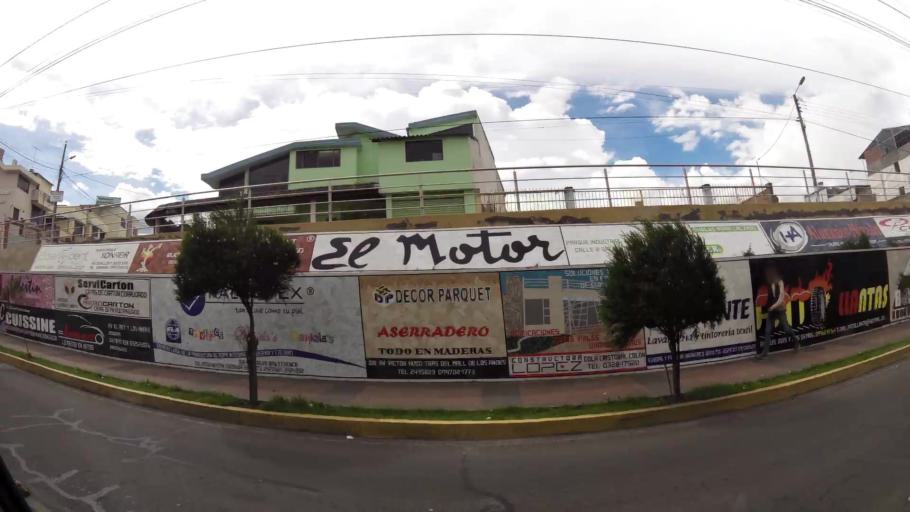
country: EC
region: Tungurahua
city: Ambato
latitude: -1.2685
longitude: -78.6290
